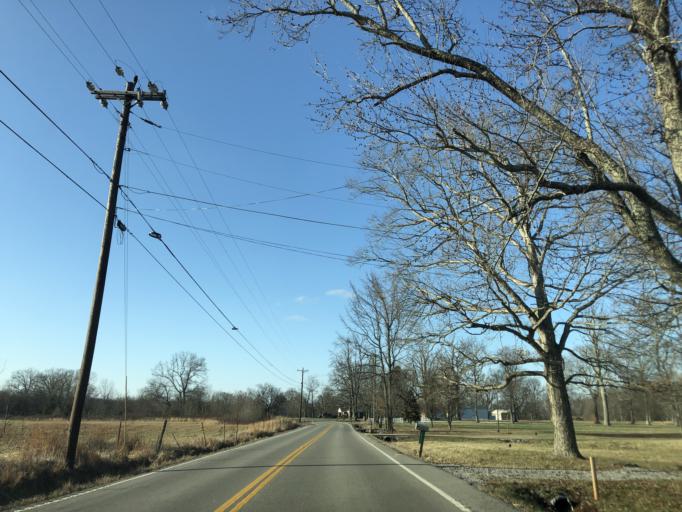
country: US
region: Tennessee
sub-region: Sumner County
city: White House
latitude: 36.4860
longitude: -86.5820
